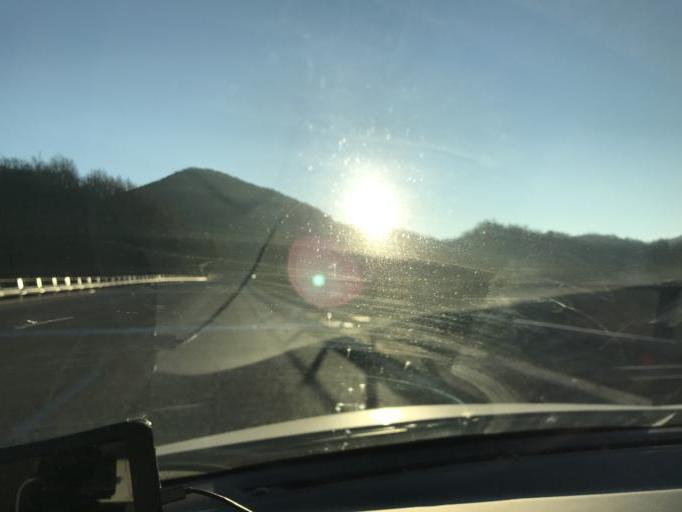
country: IT
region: Latium
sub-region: Provincia di Rieti
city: Concerviano
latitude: 42.3171
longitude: 13.0279
